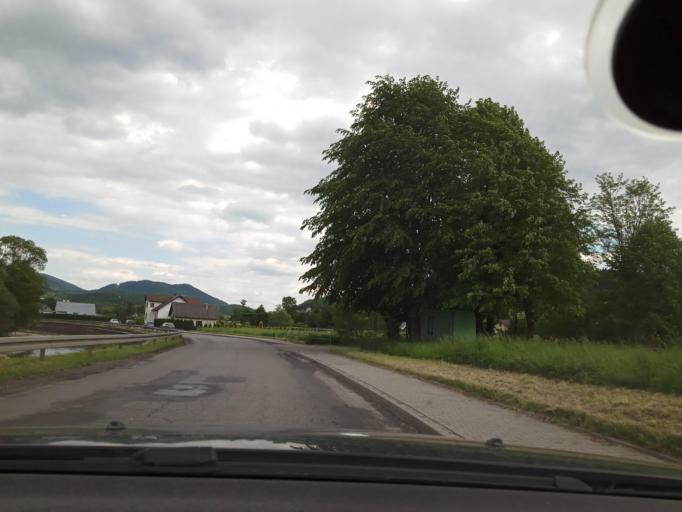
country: PL
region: Lesser Poland Voivodeship
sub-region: Powiat limanowski
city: Tymbark
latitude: 49.7404
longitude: 20.3738
